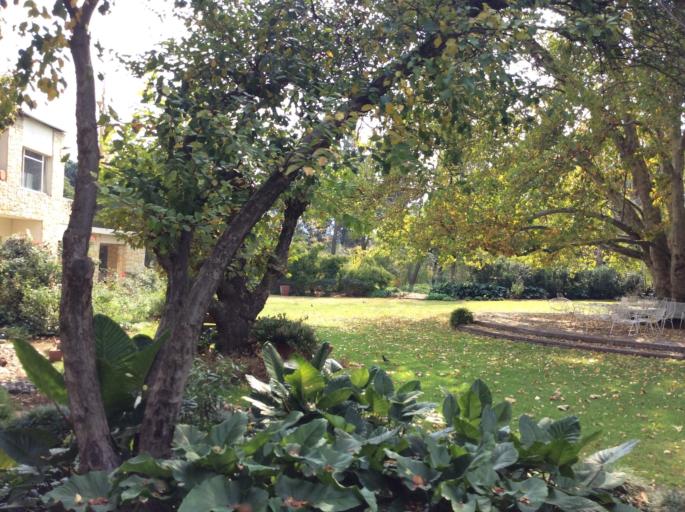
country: LS
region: Mafeteng
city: Mafeteng
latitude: -29.7268
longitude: 27.0364
